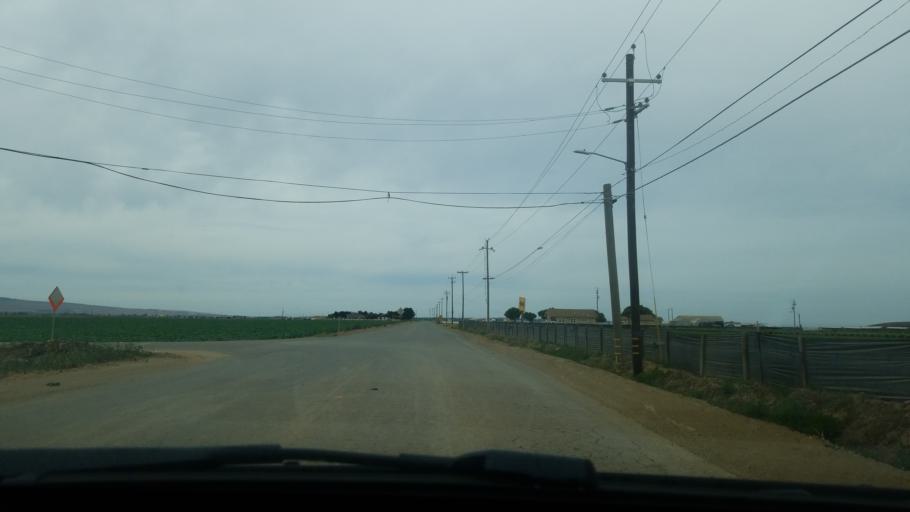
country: US
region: California
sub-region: San Luis Obispo County
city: Nipomo
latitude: 35.0036
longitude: -120.5186
